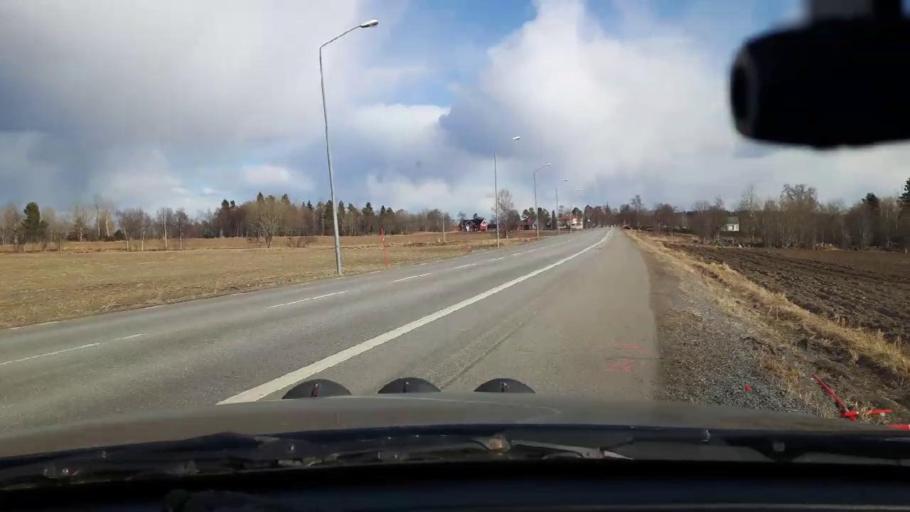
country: SE
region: Jaemtland
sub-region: OEstersunds Kommun
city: Ostersund
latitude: 63.1826
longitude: 14.5112
